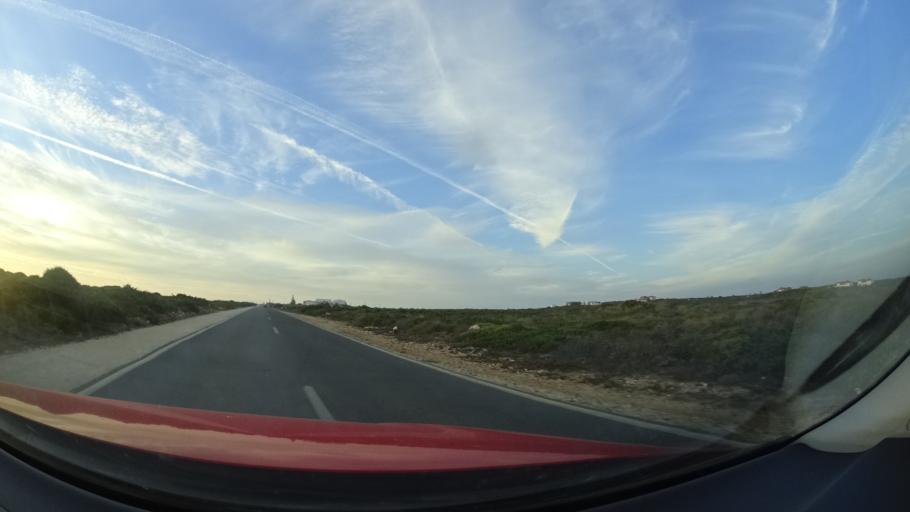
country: PT
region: Faro
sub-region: Vila do Bispo
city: Sagres
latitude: 37.0225
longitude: -8.9601
